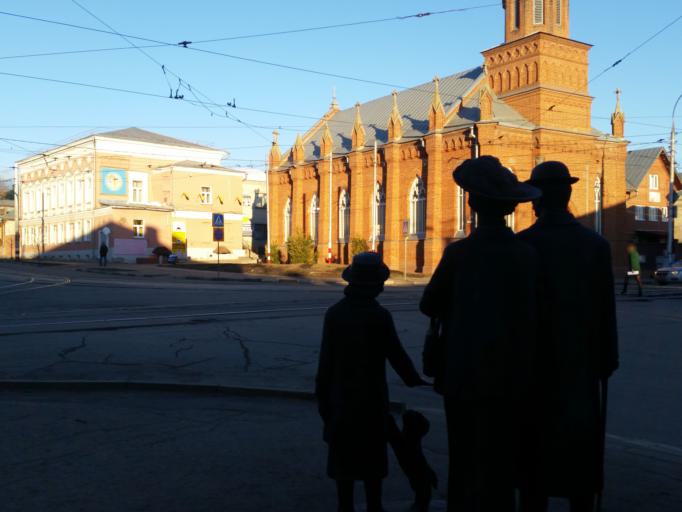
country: RU
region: Ulyanovsk
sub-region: Ulyanovskiy Rayon
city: Ulyanovsk
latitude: 54.3132
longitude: 48.3869
